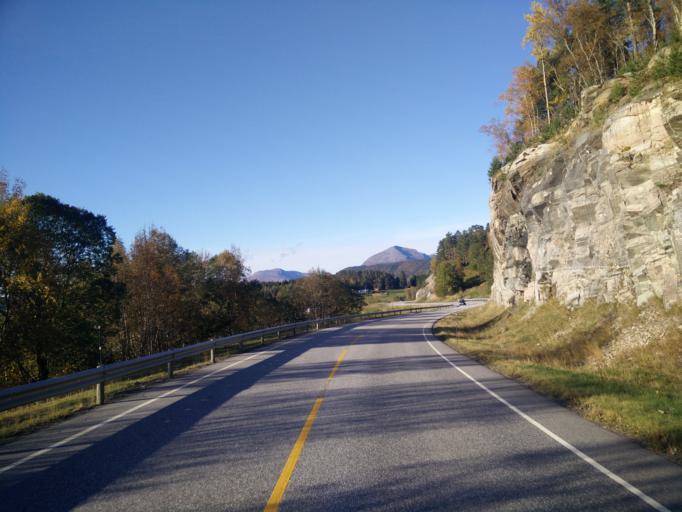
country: NO
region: More og Romsdal
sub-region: Halsa
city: Liaboen
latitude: 63.0960
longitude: 8.3465
